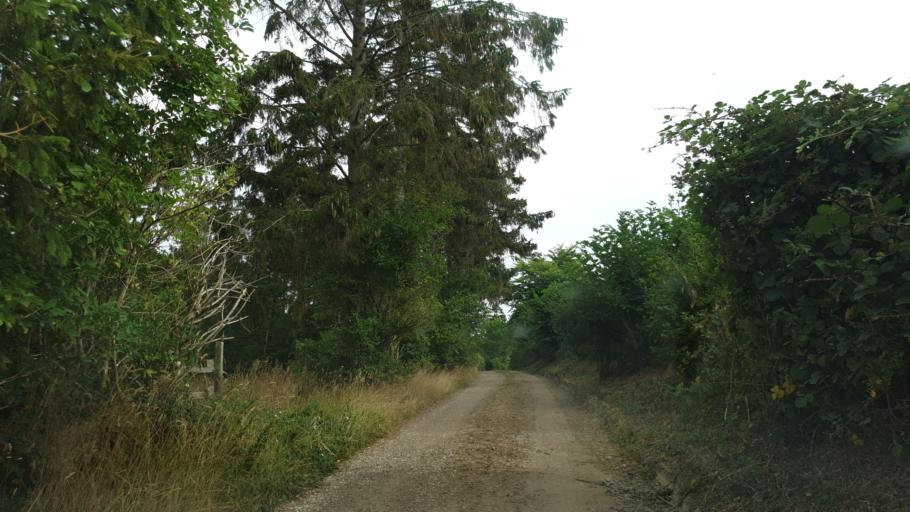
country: DK
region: Zealand
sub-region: Odsherred Kommune
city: Hojby
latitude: 55.9349
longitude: 11.6227
